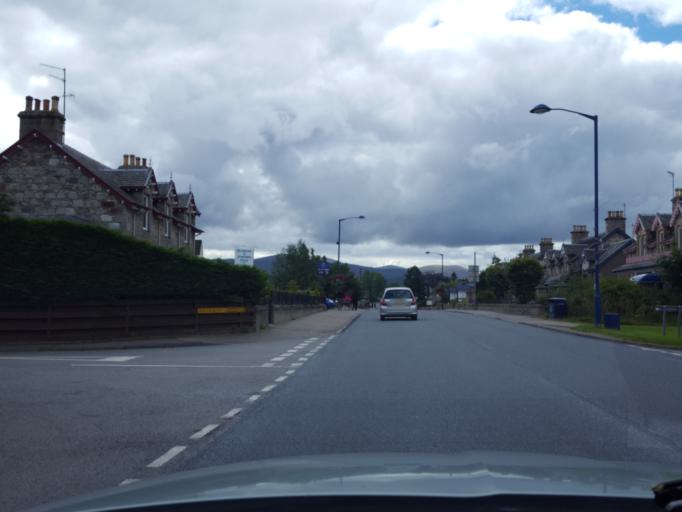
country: GB
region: Scotland
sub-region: Highland
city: Aviemore
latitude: 57.1968
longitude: -3.8290
